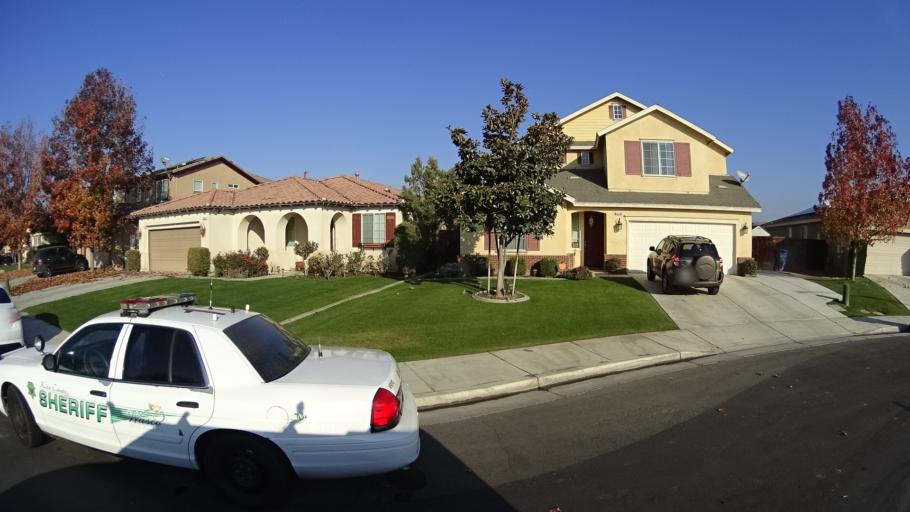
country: US
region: California
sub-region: Kern County
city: Greenacres
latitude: 35.3002
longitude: -119.1155
